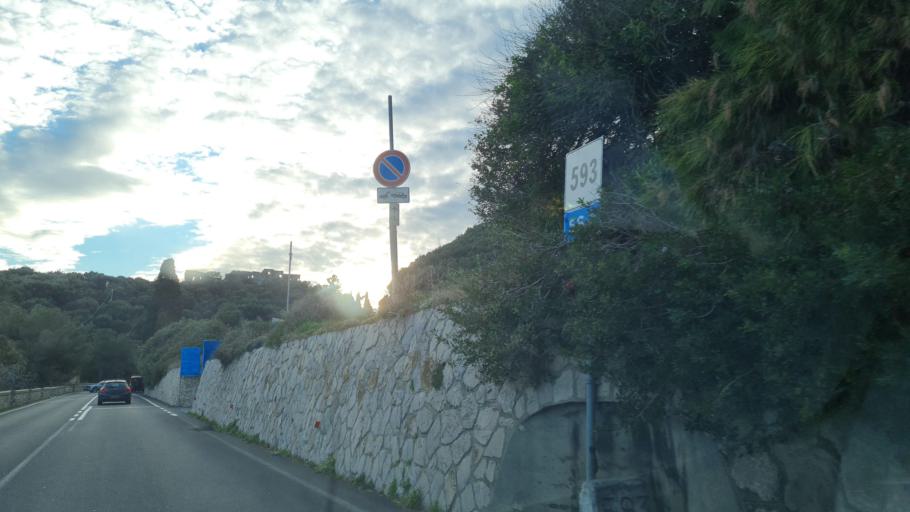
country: IT
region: Liguria
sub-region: Provincia di Savona
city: Noli
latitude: 44.1850
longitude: 8.4068
